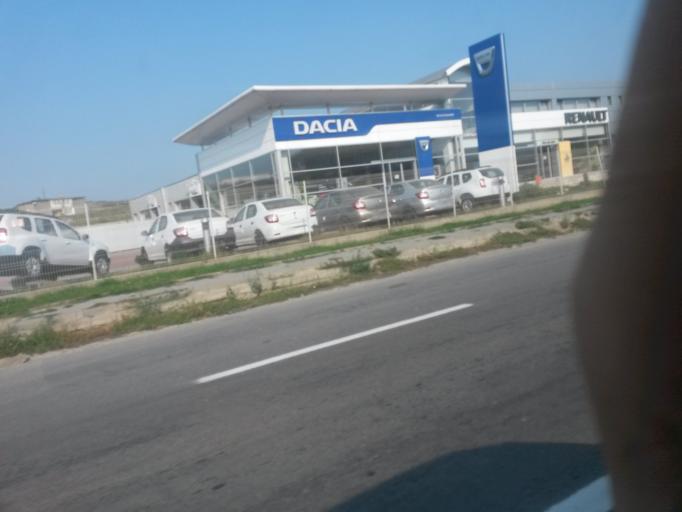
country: RO
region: Cluj
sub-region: Comuna Sandulesti
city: Copaceni
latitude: 46.5865
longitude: 23.7592
